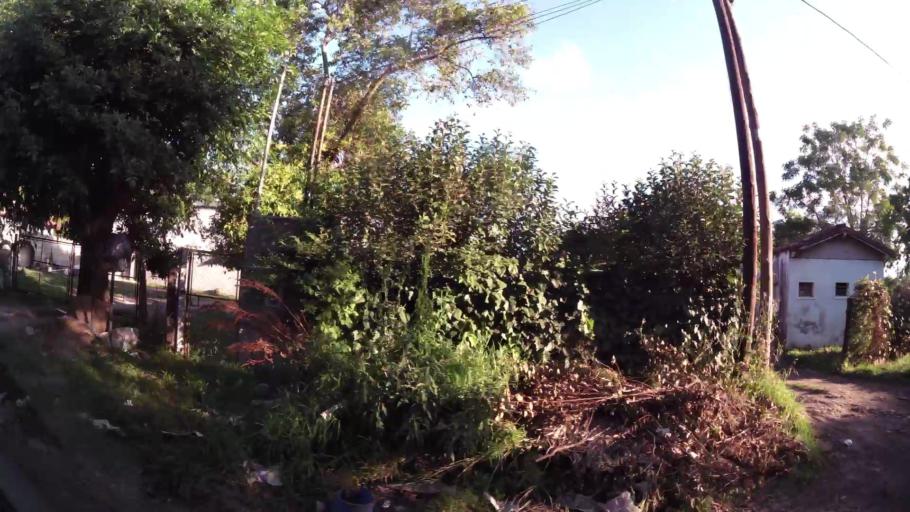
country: AR
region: Buenos Aires
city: Santa Catalina - Dique Lujan
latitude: -34.4669
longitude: -58.7519
